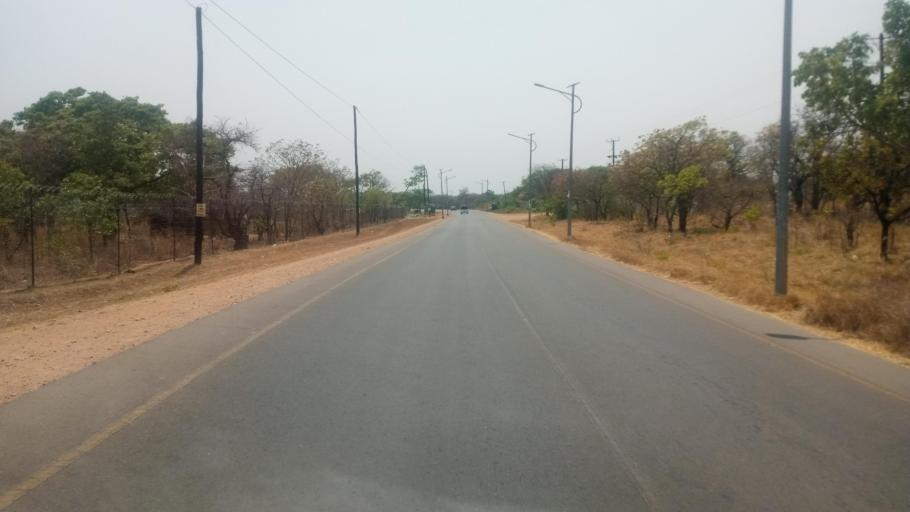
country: ZM
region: Lusaka
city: Lusaka
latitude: -15.4764
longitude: 28.4201
